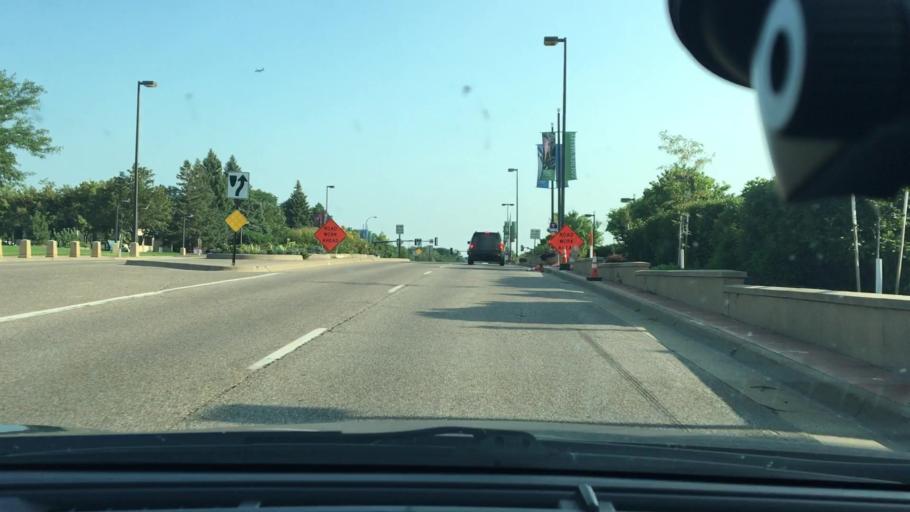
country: US
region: Minnesota
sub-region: Hennepin County
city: Golden Valley
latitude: 44.9873
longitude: -93.3805
